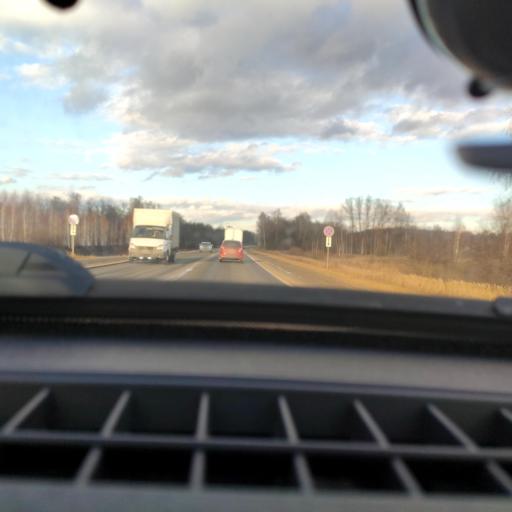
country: RU
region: Bashkortostan
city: Kabakovo
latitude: 54.7194
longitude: 56.2370
